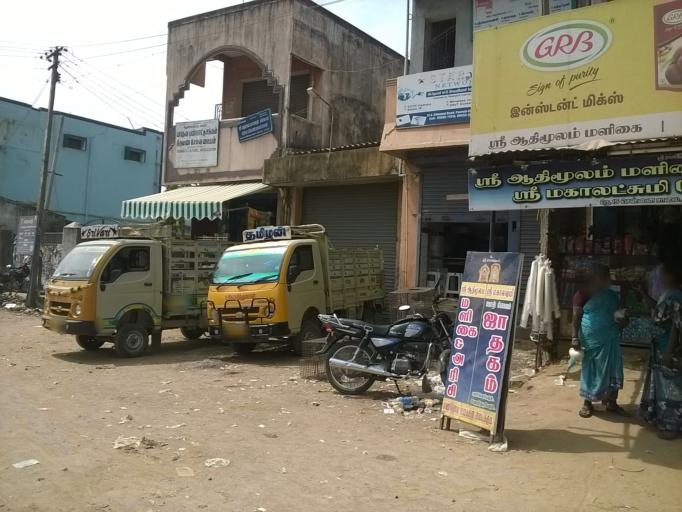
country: IN
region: Tamil Nadu
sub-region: Cuddalore
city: Panruti
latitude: 11.7745
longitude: 79.5523
